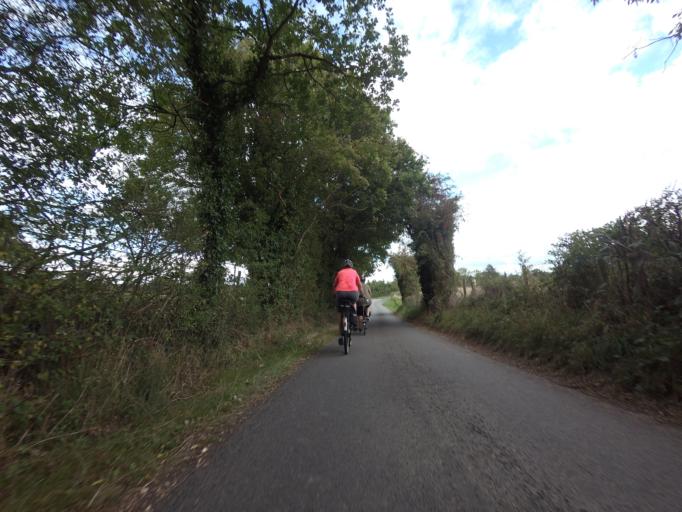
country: GB
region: England
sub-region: Kent
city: Marden
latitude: 51.2140
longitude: 0.5197
